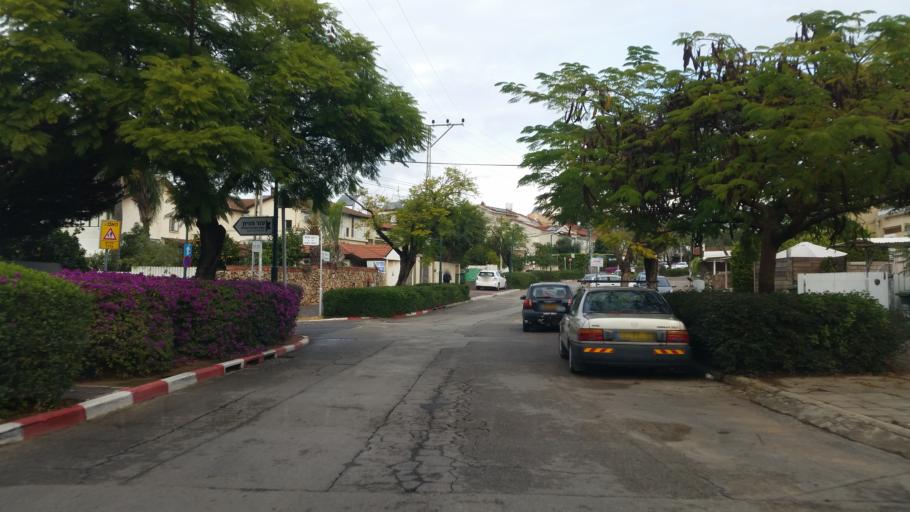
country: IL
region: Tel Aviv
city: Ramat HaSharon
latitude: 32.1649
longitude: 34.8556
